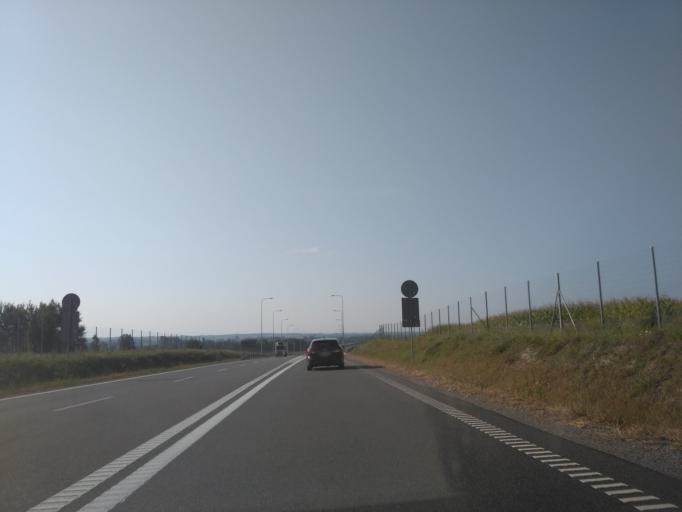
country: PL
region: Subcarpathian Voivodeship
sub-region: Powiat rzeszowski
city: Sokolow Malopolski
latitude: 50.2377
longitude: 22.1391
